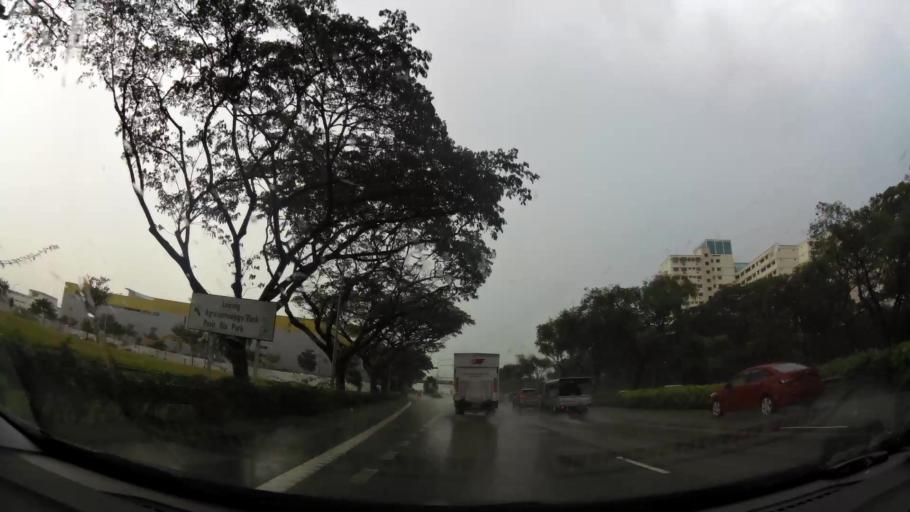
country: MY
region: Johor
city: Kampung Pasir Gudang Baru
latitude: 1.3739
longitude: 103.9357
